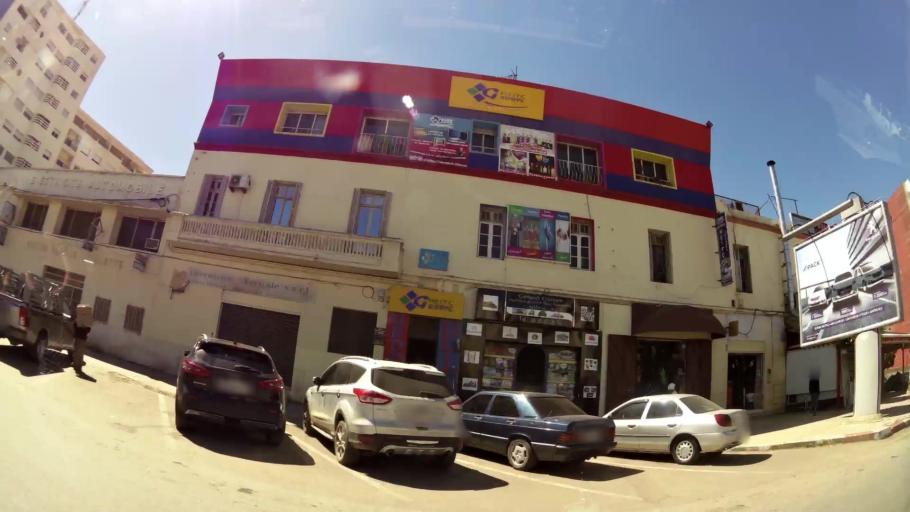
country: MA
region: Meknes-Tafilalet
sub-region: Meknes
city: Meknes
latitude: 33.8974
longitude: -5.5391
